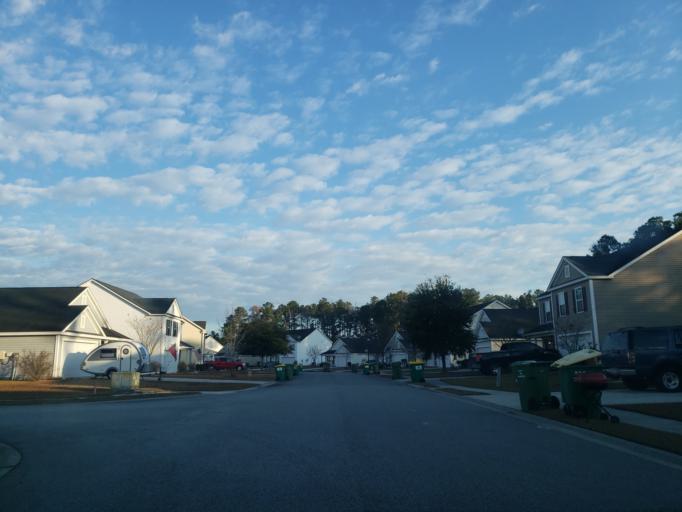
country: US
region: Georgia
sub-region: Chatham County
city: Bloomingdale
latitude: 32.1521
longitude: -81.2697
